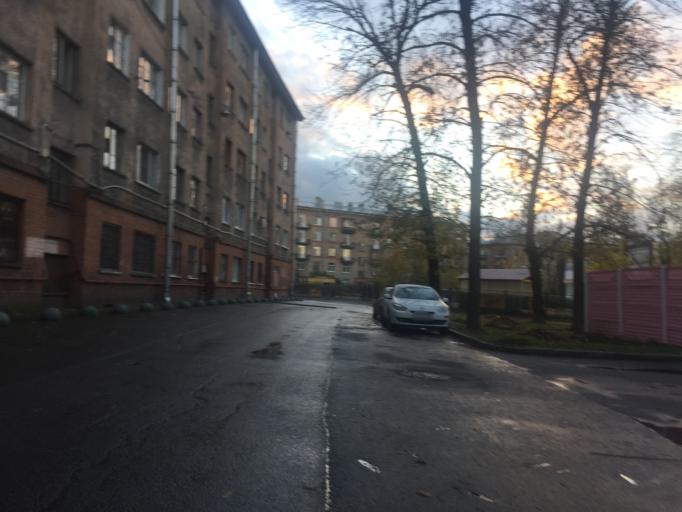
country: RU
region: St.-Petersburg
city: Obukhovo
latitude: 59.8788
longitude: 30.4335
